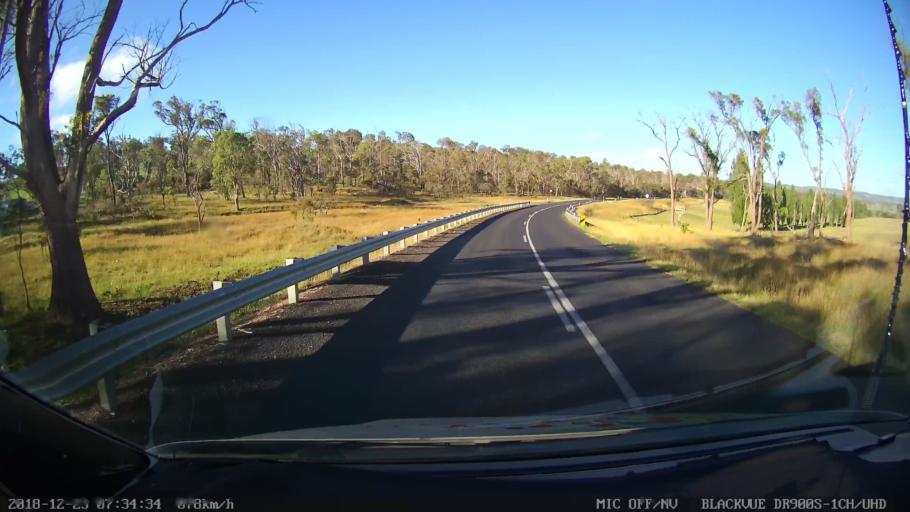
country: AU
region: New South Wales
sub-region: Armidale Dumaresq
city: Enmore
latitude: -30.5212
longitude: 152.0923
